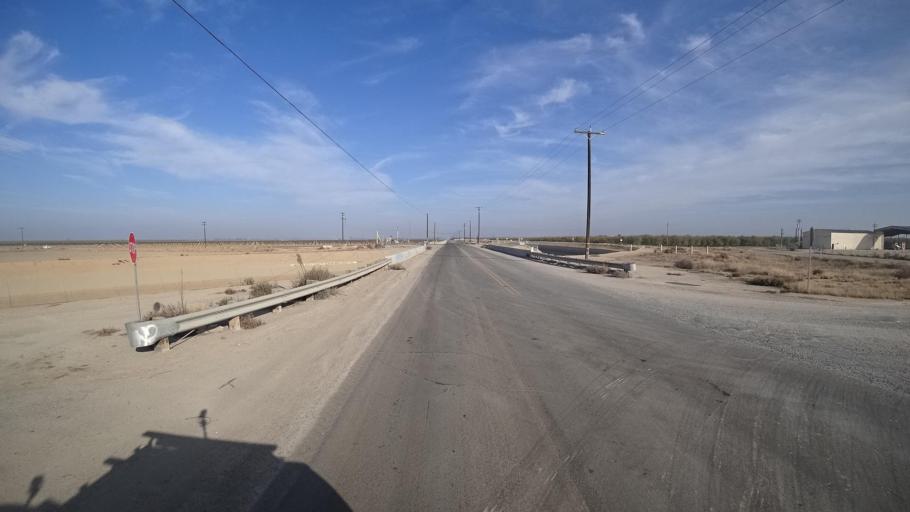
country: US
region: California
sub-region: Kern County
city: McFarland
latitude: 35.6445
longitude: -119.2045
